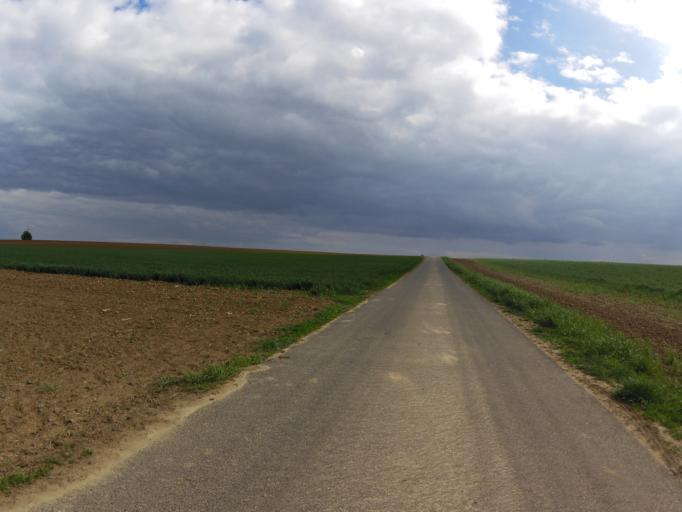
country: DE
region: Bavaria
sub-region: Regierungsbezirk Unterfranken
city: Oberpleichfeld
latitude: 49.8609
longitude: 10.0822
